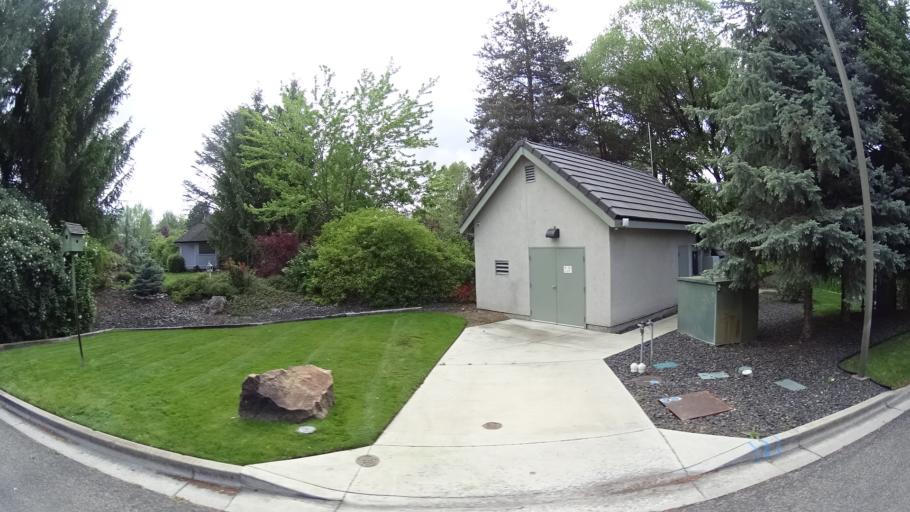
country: US
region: Idaho
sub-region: Ada County
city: Eagle
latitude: 43.6681
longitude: -116.2974
